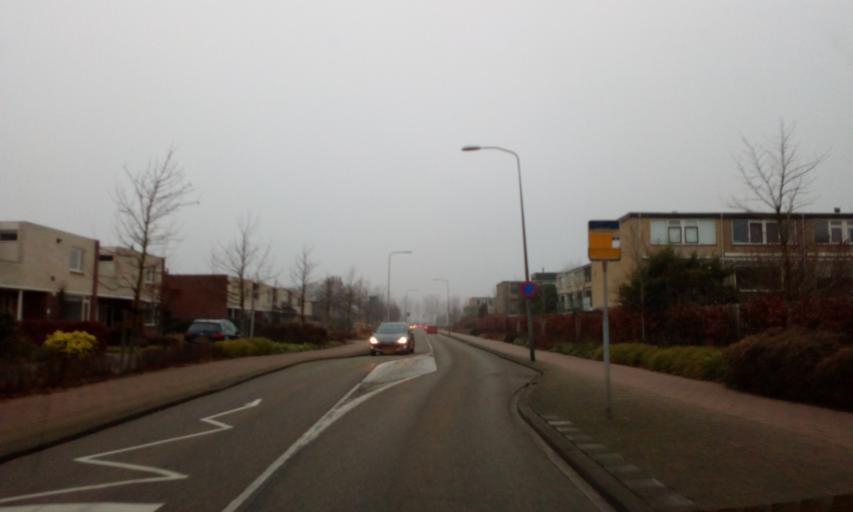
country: NL
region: South Holland
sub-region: Gemeente Capelle aan den IJssel
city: Capelle aan den IJssel
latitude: 51.9639
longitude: 4.6030
